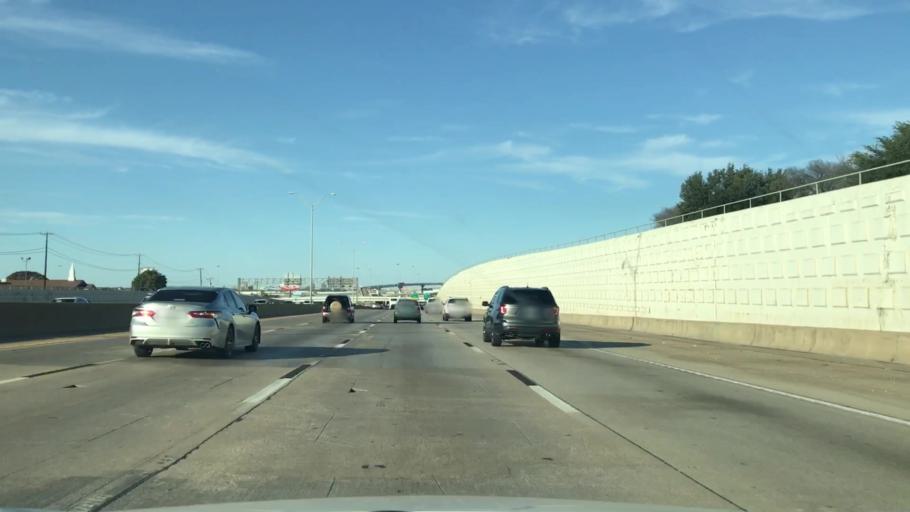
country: US
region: Texas
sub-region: Tarrant County
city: Edgecliff Village
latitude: 32.6559
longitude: -97.3212
